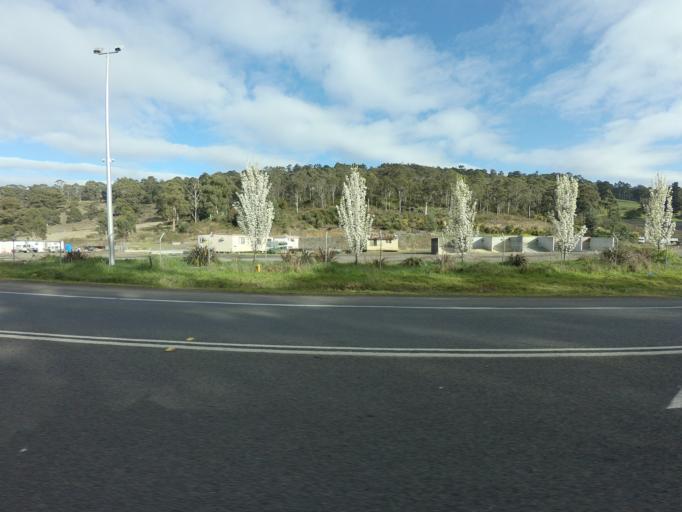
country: AU
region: Tasmania
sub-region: Huon Valley
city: Huonville
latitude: -43.0512
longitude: 147.0379
